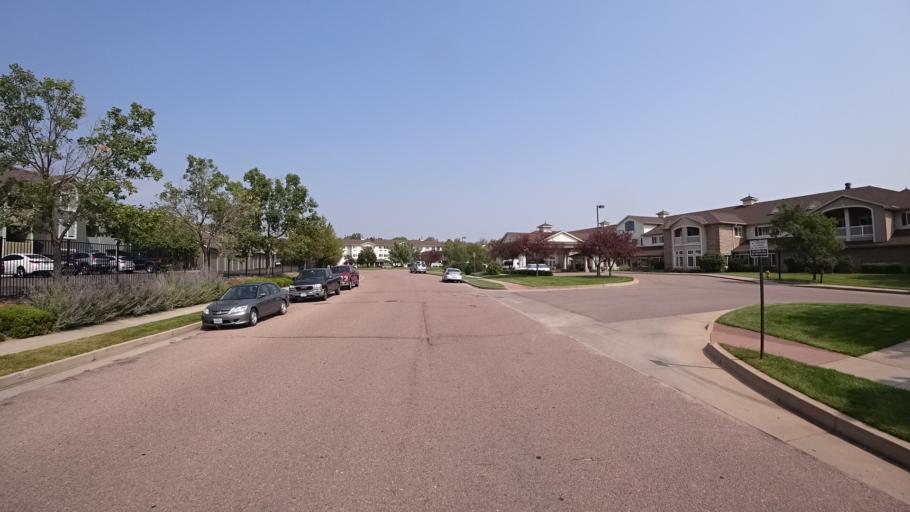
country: US
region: Colorado
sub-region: El Paso County
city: Colorado Springs
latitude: 38.8285
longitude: -104.7827
